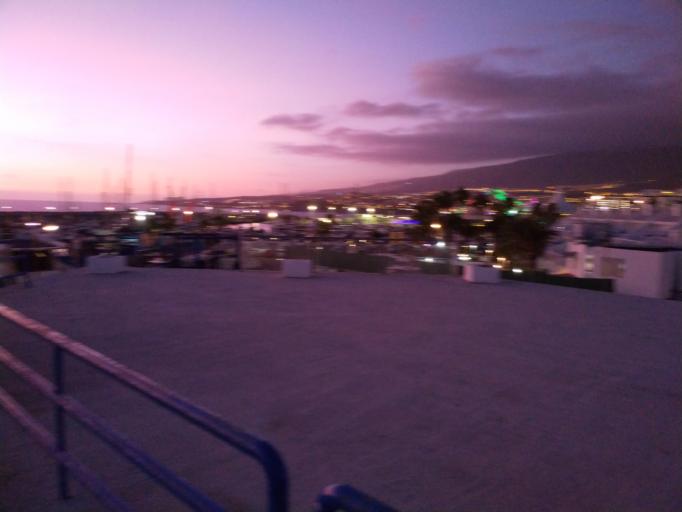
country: ES
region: Canary Islands
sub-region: Provincia de Santa Cruz de Tenerife
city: Playa de las Americas
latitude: 28.0767
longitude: -16.7359
